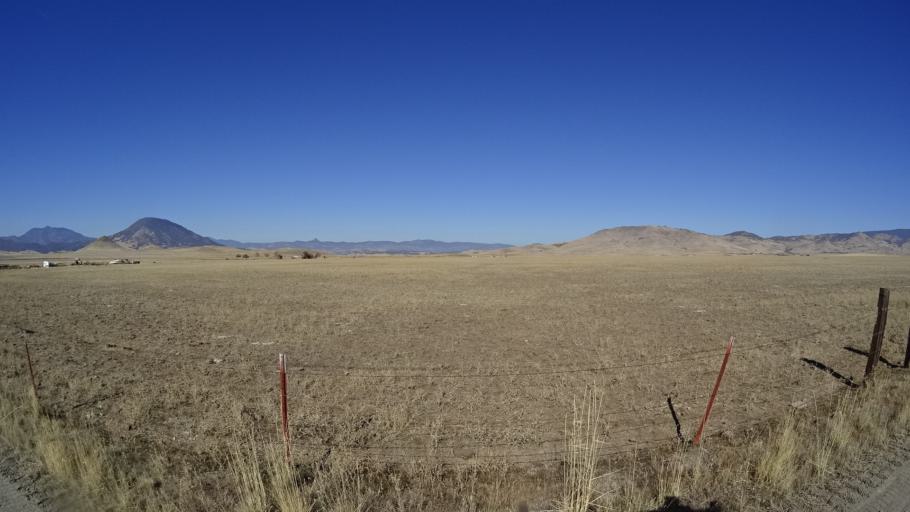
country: US
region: California
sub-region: Siskiyou County
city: Montague
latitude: 41.7938
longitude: -122.4288
